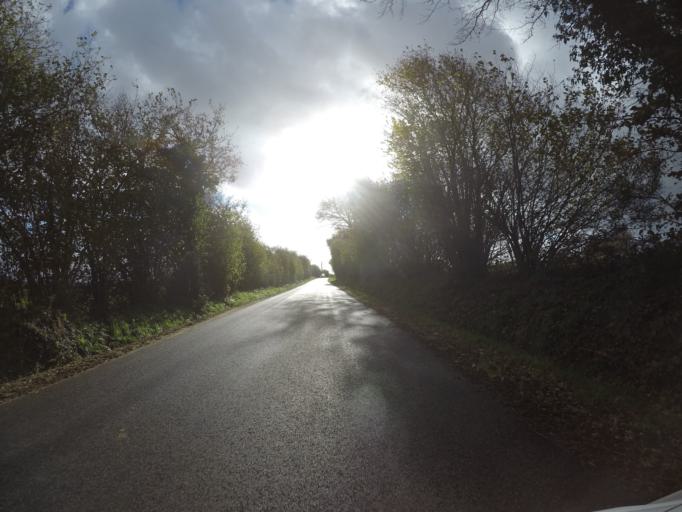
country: FR
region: Brittany
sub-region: Departement des Cotes-d'Armor
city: Bourbriac
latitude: 48.4984
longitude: -3.1881
